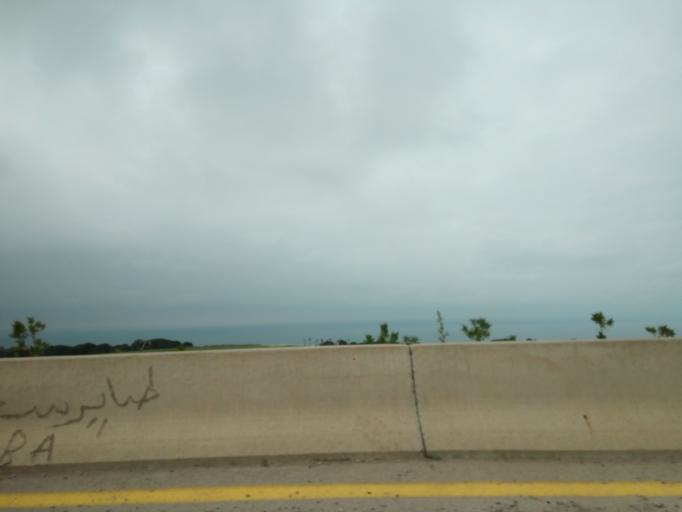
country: DZ
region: Tipaza
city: Tipasa
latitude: 36.5771
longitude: 2.5011
